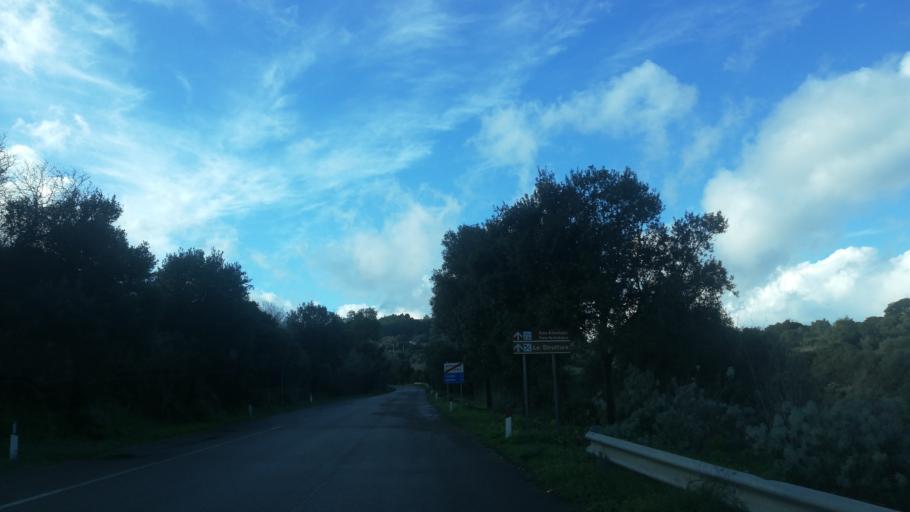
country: IT
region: Sardinia
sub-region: Provincia di Medio Campidano
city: Villanovaforru
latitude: 39.6333
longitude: 8.8631
